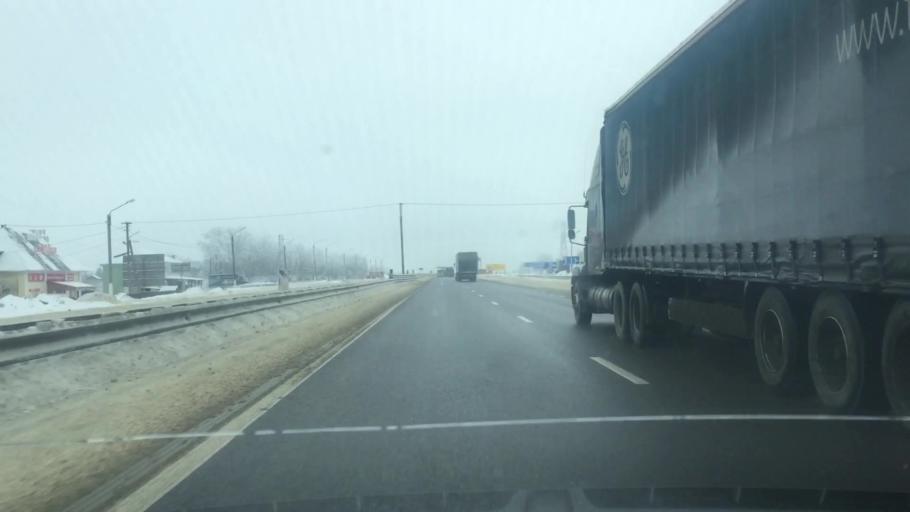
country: RU
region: Tula
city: Kazachka
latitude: 53.3080
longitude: 38.1788
